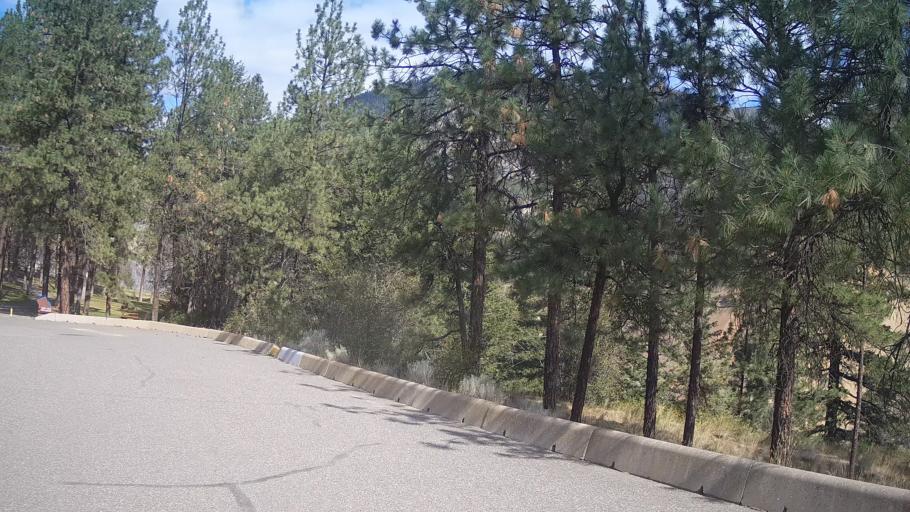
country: CA
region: British Columbia
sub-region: Thompson-Nicola Regional District
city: Ashcroft
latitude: 50.2543
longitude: -121.5094
